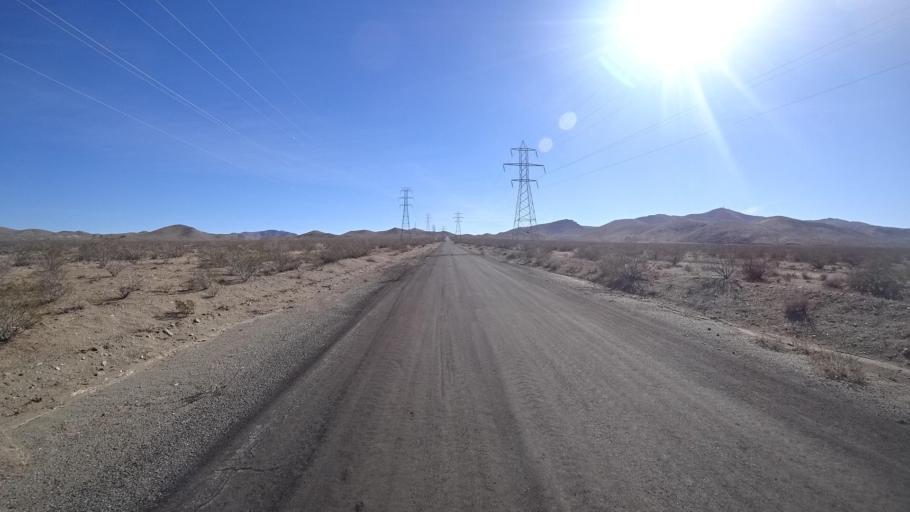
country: US
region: California
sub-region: Kern County
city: Ridgecrest
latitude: 35.3896
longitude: -117.6672
